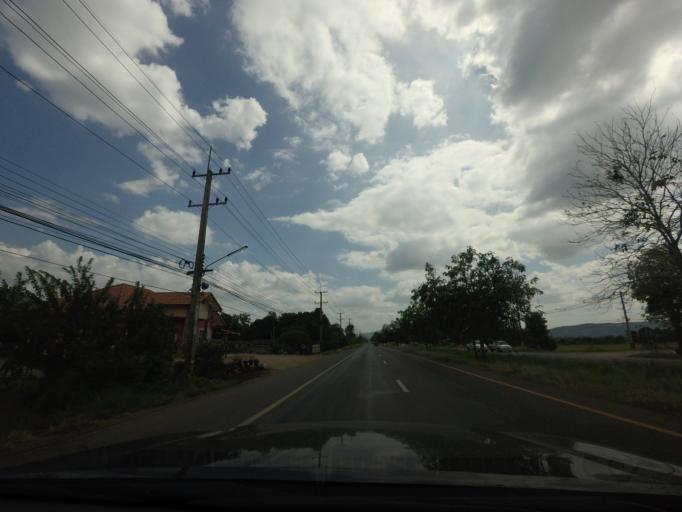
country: TH
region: Phetchabun
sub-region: Amphoe Bueng Sam Phan
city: Bueng Sam Phan
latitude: 15.7486
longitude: 101.0130
